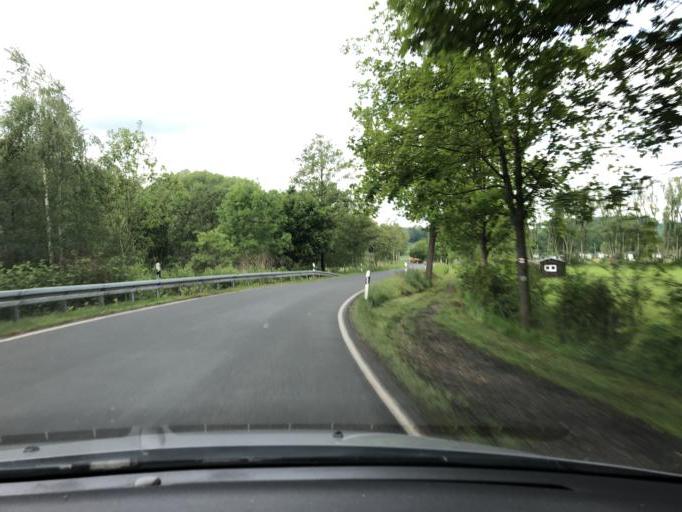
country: DE
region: Saxony
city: Remse
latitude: 50.8562
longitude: 12.5862
